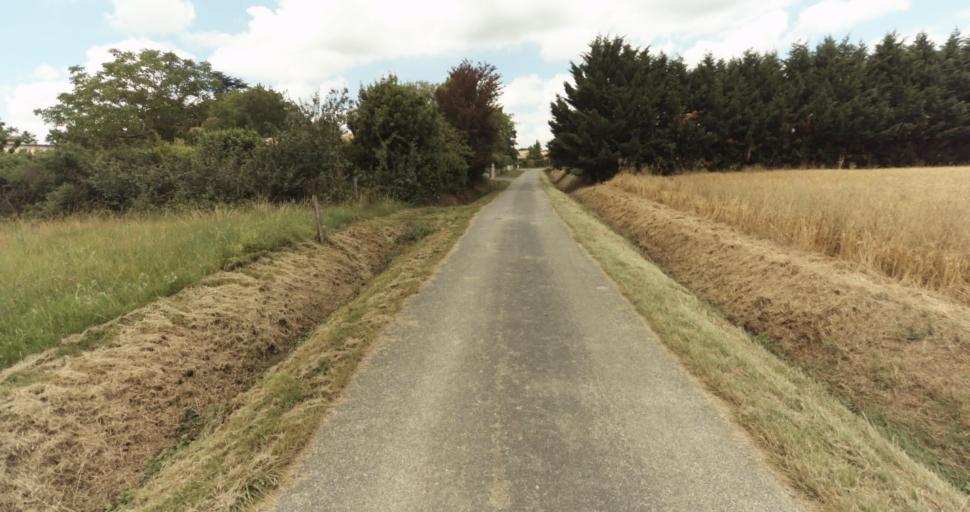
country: FR
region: Midi-Pyrenees
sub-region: Departement de la Haute-Garonne
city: Fontenilles
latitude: 43.5493
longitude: 1.1758
